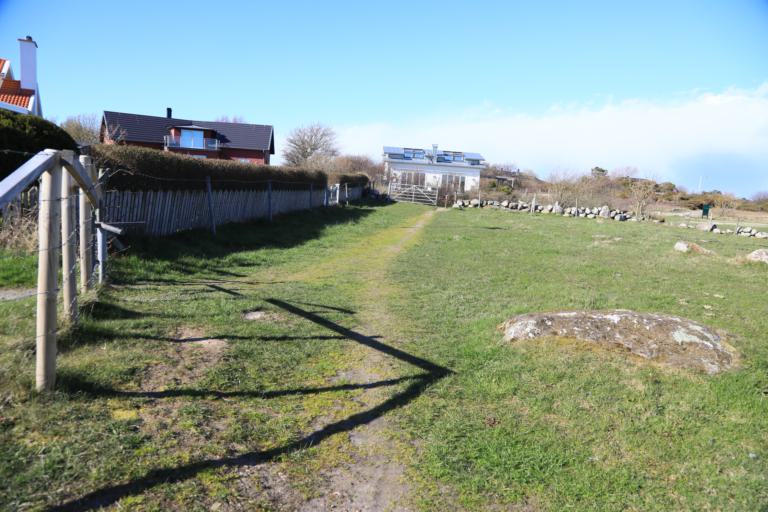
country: SE
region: Halland
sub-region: Varbergs Kommun
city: Traslovslage
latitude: 57.0661
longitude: 12.2580
